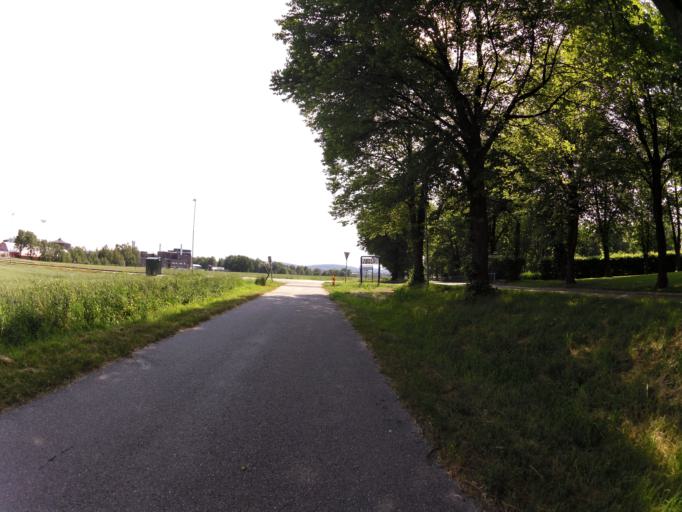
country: NO
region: Ostfold
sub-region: Sarpsborg
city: Sarpsborg
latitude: 59.2739
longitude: 11.1090
